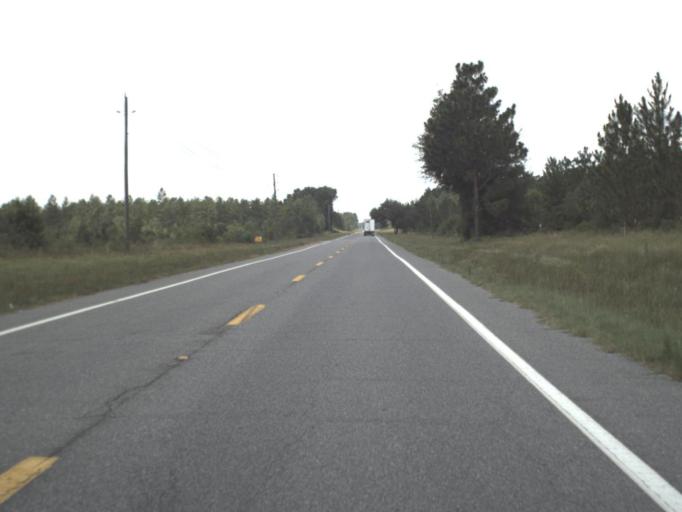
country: US
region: Florida
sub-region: Madison County
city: Madison
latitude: 30.4866
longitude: -83.1932
